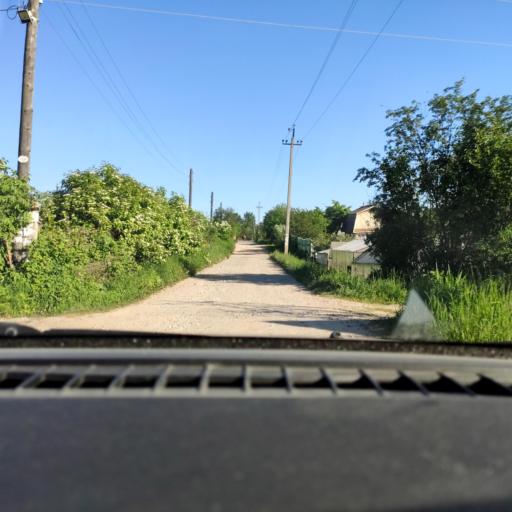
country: RU
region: Perm
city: Overyata
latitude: 58.1229
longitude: 55.8767
